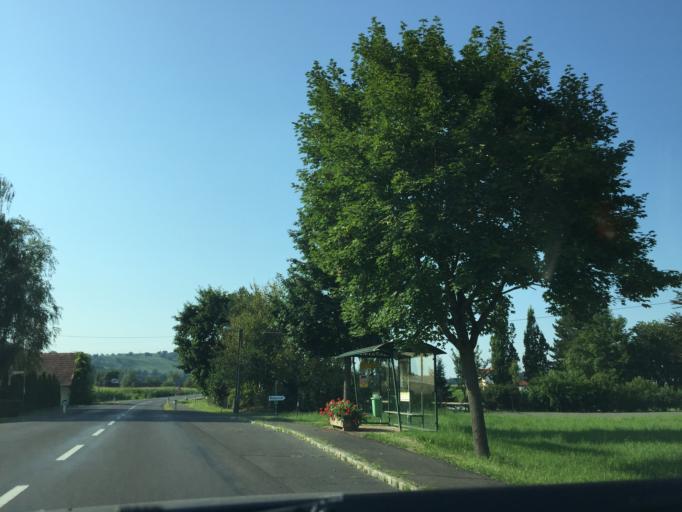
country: AT
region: Styria
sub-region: Politischer Bezirk Suedoststeiermark
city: Straden
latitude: 46.7799
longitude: 15.8577
